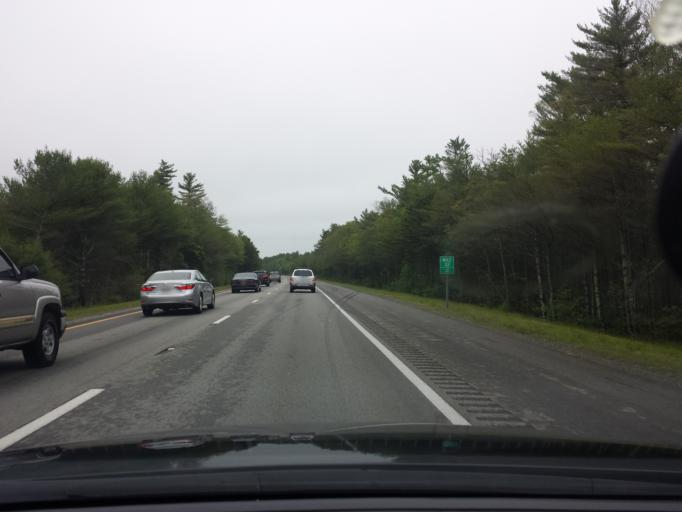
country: US
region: Massachusetts
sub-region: Plymouth County
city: Mattapoisett Center
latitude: 41.6888
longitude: -70.8064
